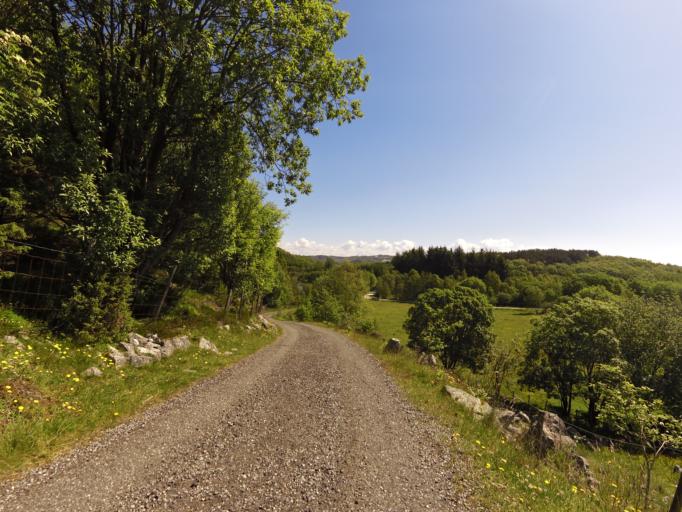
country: NO
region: Rogaland
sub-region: Eigersund
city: Egersund
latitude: 58.5029
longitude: 5.9020
